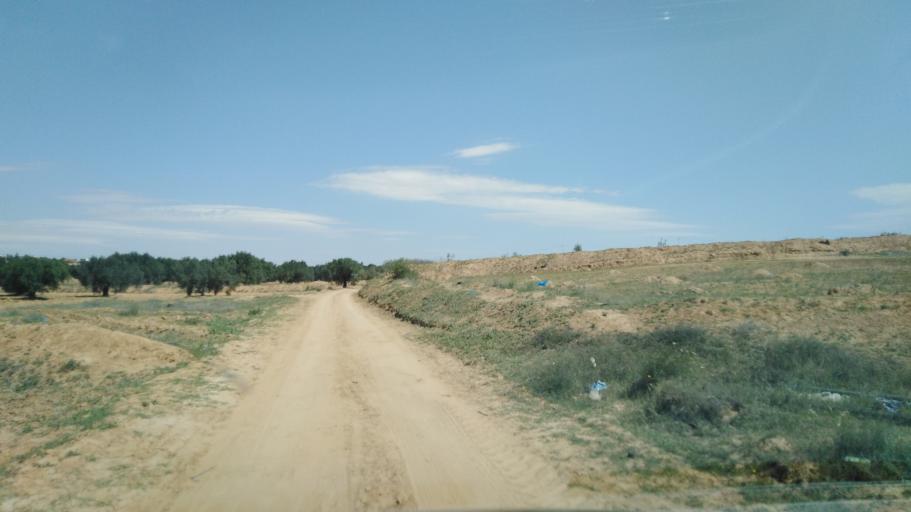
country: TN
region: Safaqis
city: Sfax
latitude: 34.7728
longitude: 10.5271
